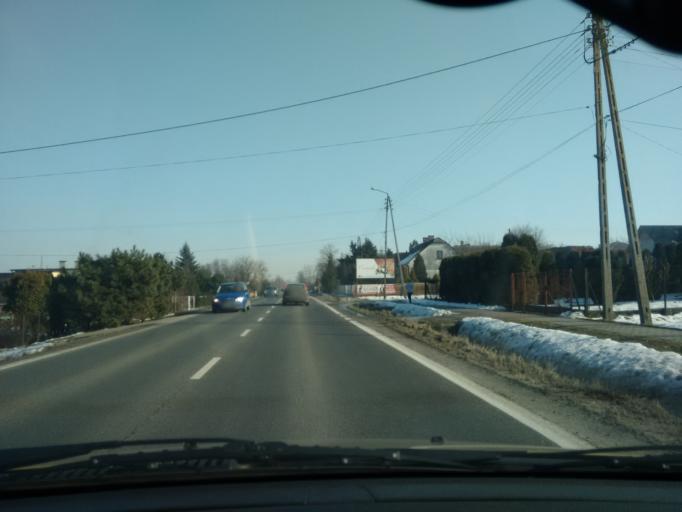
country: PL
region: Lesser Poland Voivodeship
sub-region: Powiat oswiecimski
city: Bulowice
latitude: 49.8779
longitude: 19.2747
